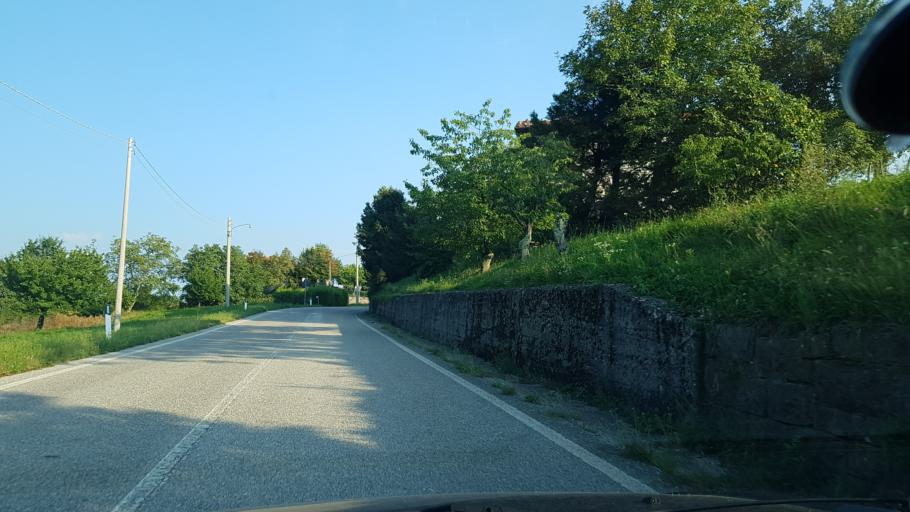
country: IT
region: Friuli Venezia Giulia
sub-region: Provincia di Gorizia
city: San Floriano del Collio
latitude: 45.9820
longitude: 13.6084
